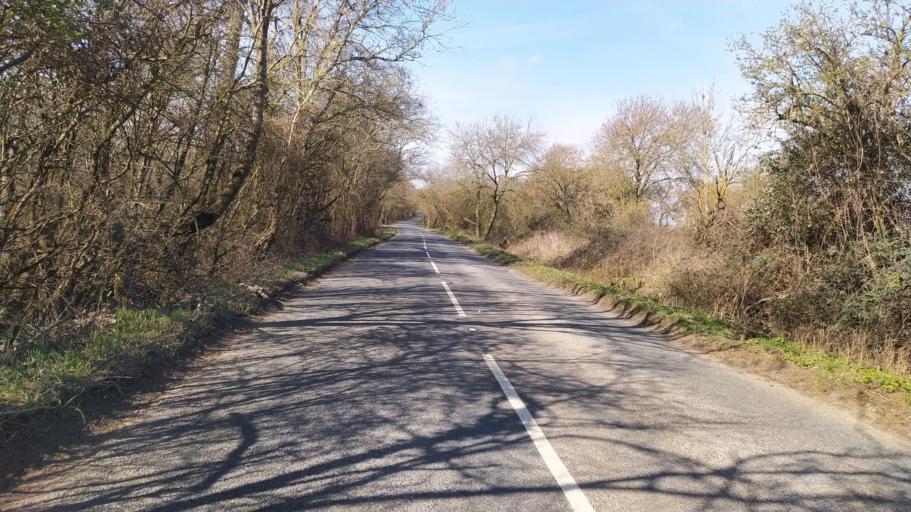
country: GB
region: England
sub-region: Somerset
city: Ilchester
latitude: 51.0160
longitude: -2.6857
